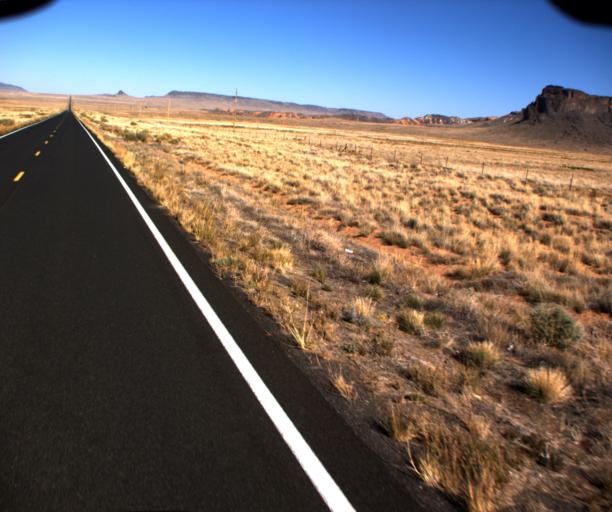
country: US
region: Arizona
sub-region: Navajo County
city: Dilkon
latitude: 35.3089
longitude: -110.4227
